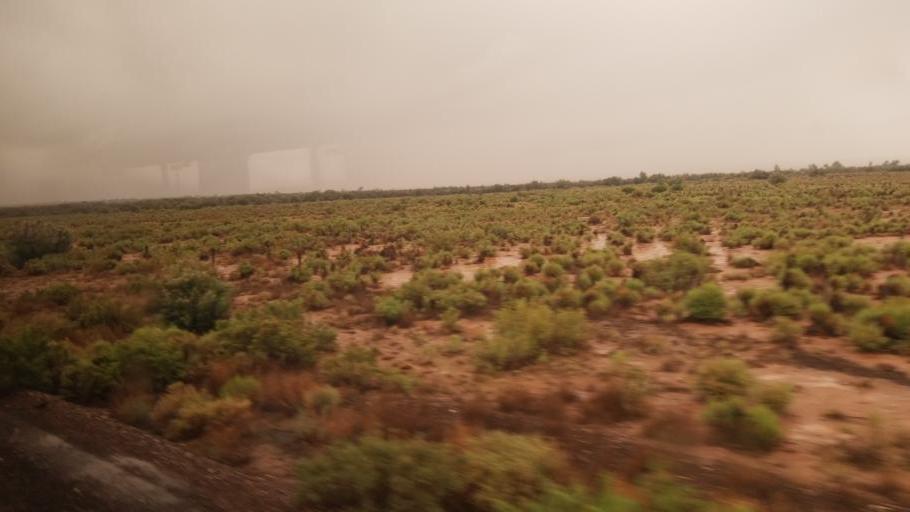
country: US
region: Arizona
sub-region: Navajo County
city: Joseph City
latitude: 34.9674
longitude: -110.4678
